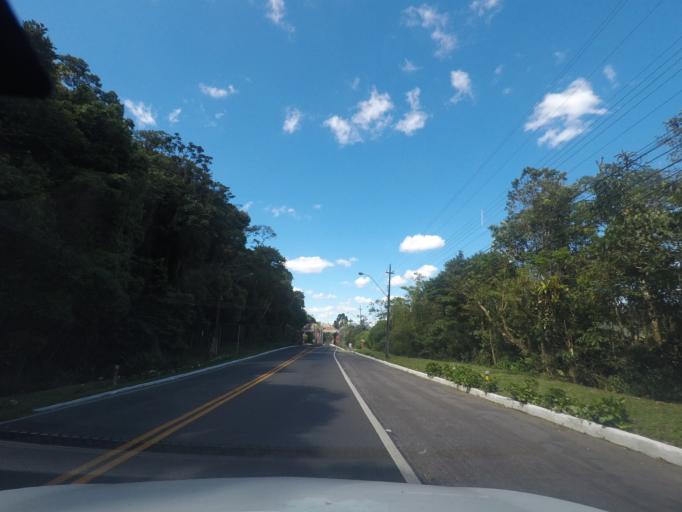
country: BR
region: Rio de Janeiro
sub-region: Teresopolis
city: Teresopolis
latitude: -22.4571
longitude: -42.9854
